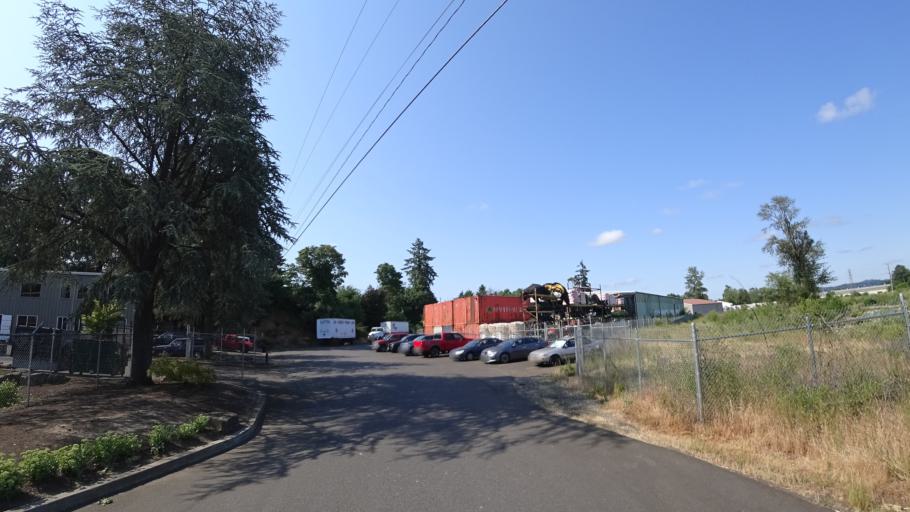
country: US
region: Oregon
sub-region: Multnomah County
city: Lents
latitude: 45.4590
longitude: -122.5845
